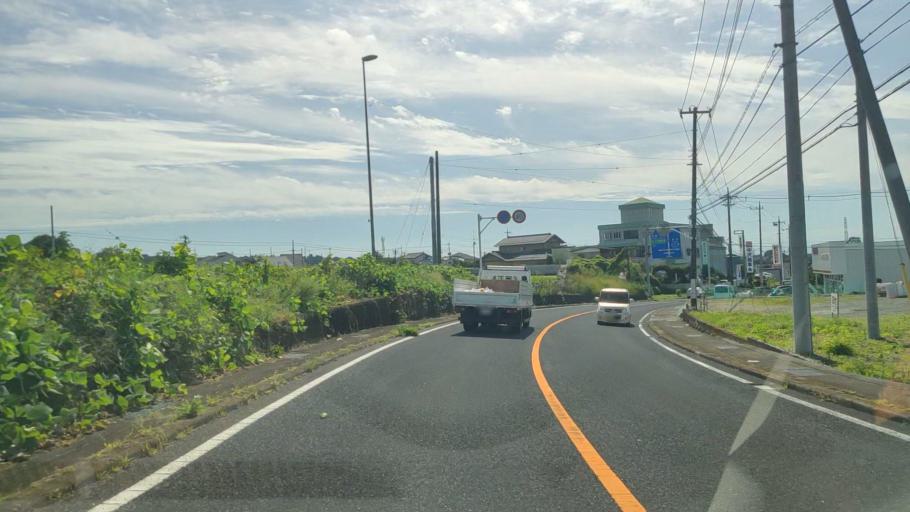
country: JP
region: Gunma
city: Shibukawa
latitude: 36.5238
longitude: 139.0113
